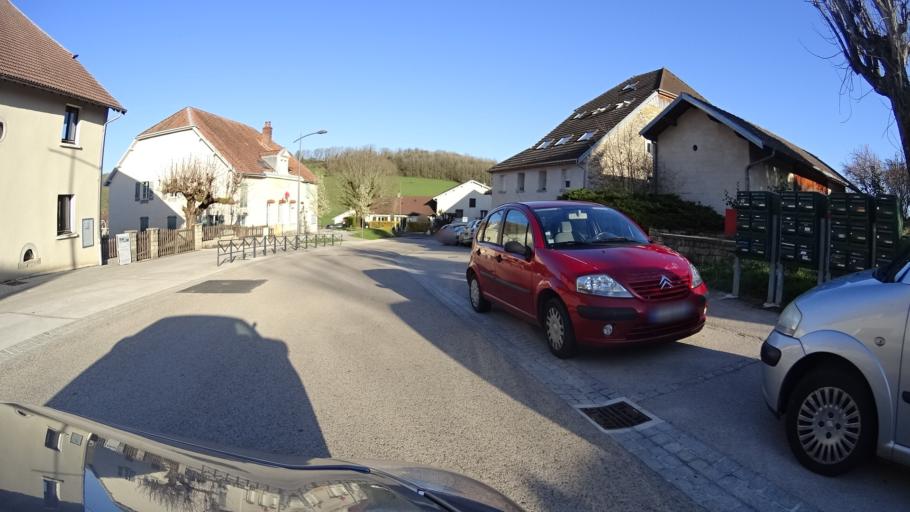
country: FR
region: Franche-Comte
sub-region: Departement du Doubs
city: Beure
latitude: 47.1845
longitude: 5.9903
